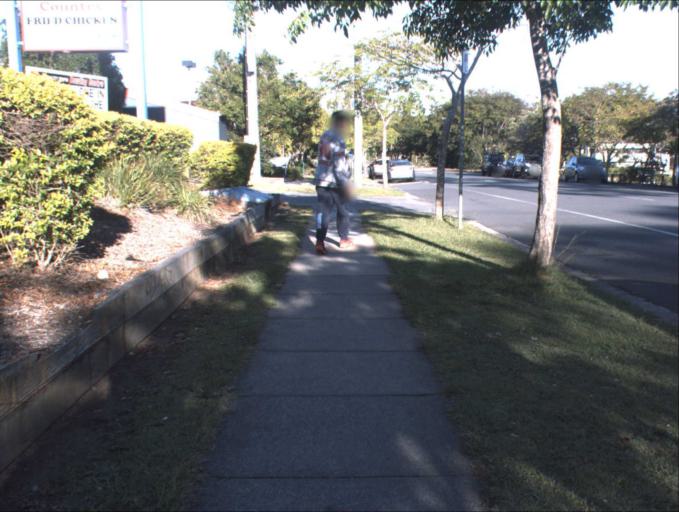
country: AU
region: Queensland
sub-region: Logan
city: Logan City
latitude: -27.6420
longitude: 153.1170
